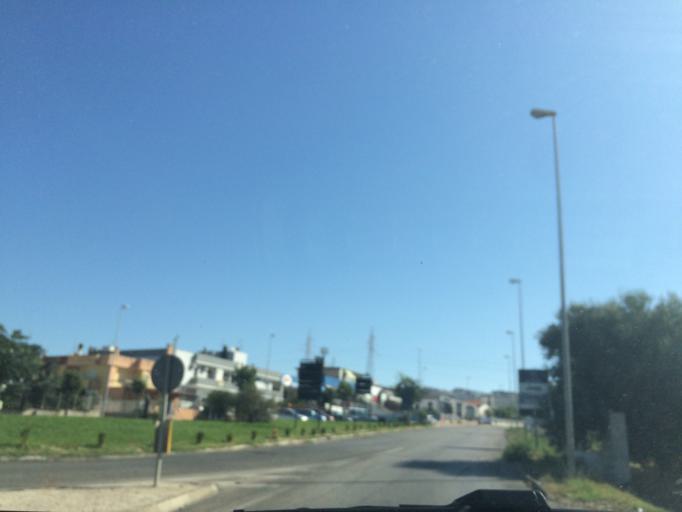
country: IT
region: Basilicate
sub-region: Provincia di Matera
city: Matera
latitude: 40.6688
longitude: 16.5741
